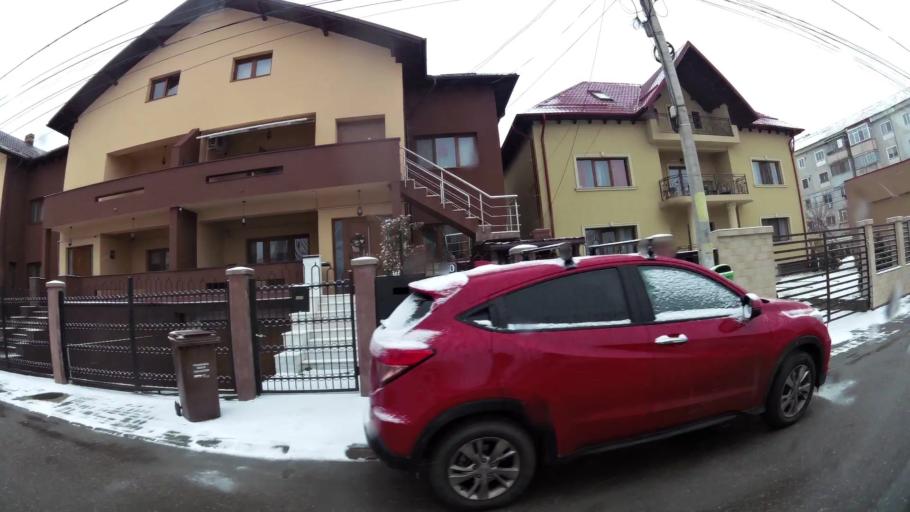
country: RO
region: Dambovita
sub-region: Municipiul Targoviste
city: Targoviste
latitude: 44.9318
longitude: 25.4415
